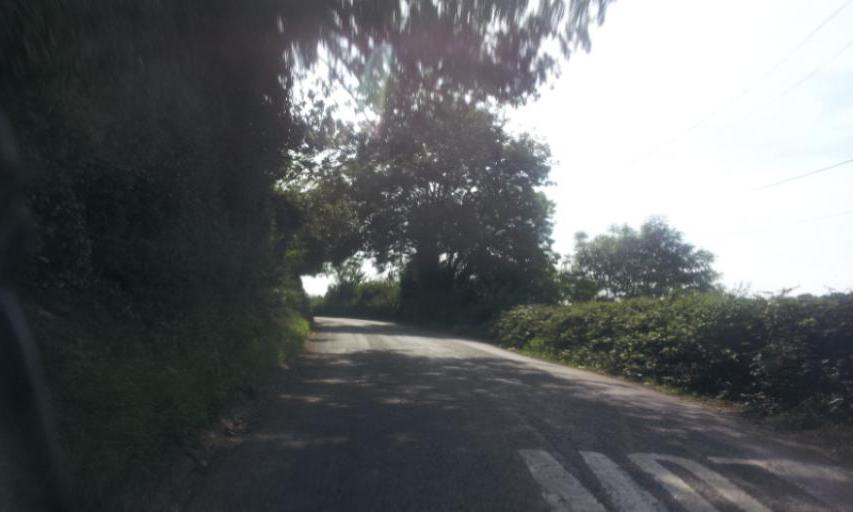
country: GB
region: England
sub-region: Kent
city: Newington
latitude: 51.3401
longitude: 0.6951
